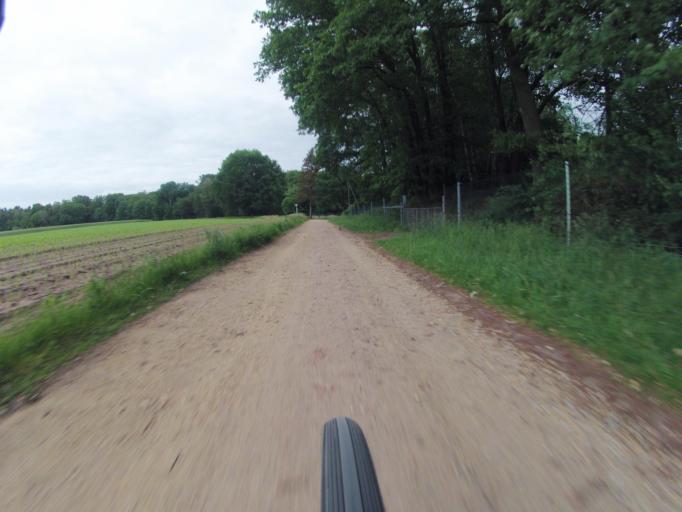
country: DE
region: North Rhine-Westphalia
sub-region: Regierungsbezirk Munster
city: Dreierwalde
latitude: 52.2444
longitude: 7.5313
